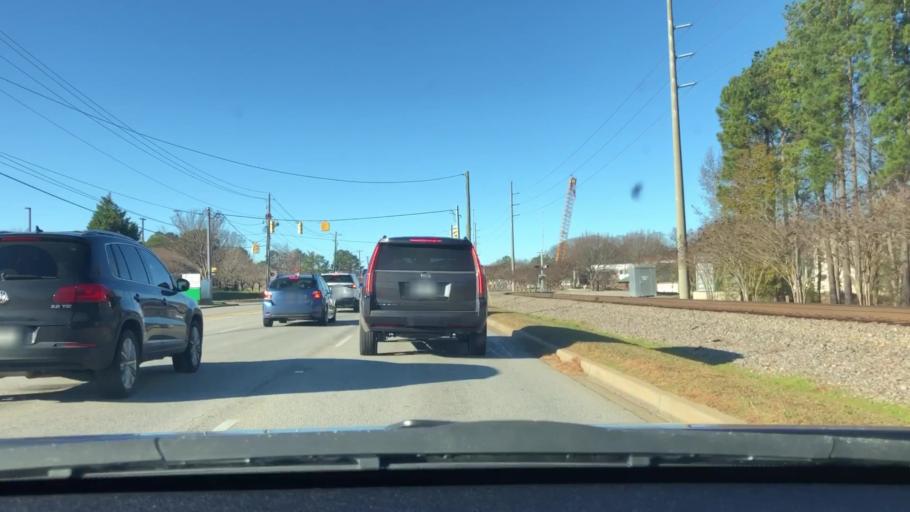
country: US
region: South Carolina
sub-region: Lexington County
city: Irmo
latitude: 34.0776
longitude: -81.1785
